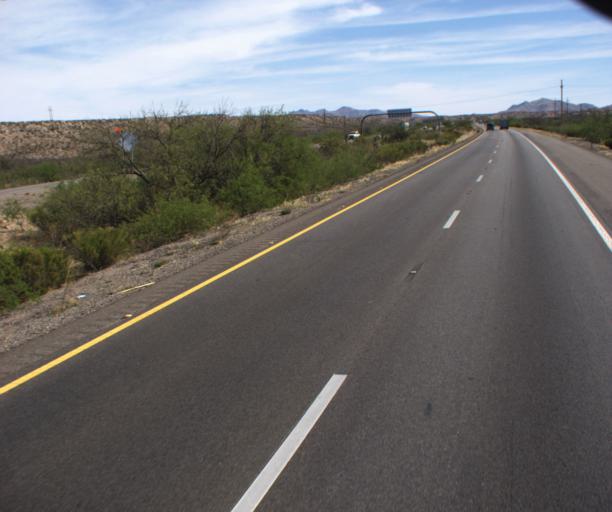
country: US
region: Arizona
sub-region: Cochise County
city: Benson
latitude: 31.9701
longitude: -110.2409
